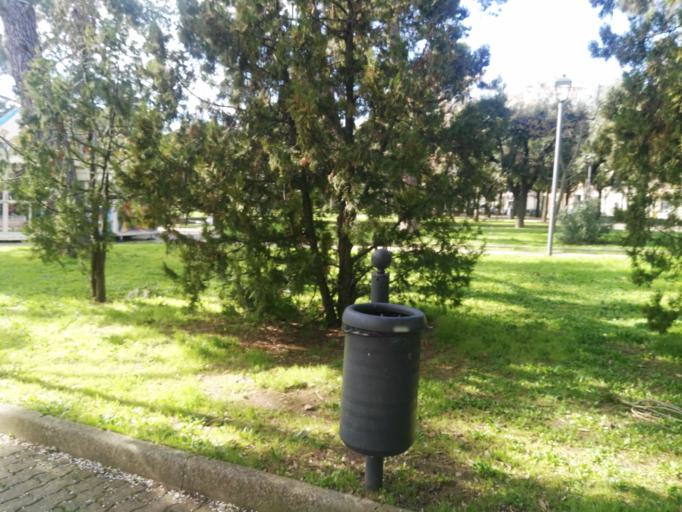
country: IT
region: Apulia
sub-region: Provincia di Bari
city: Bitonto
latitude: 41.1134
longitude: 16.6970
